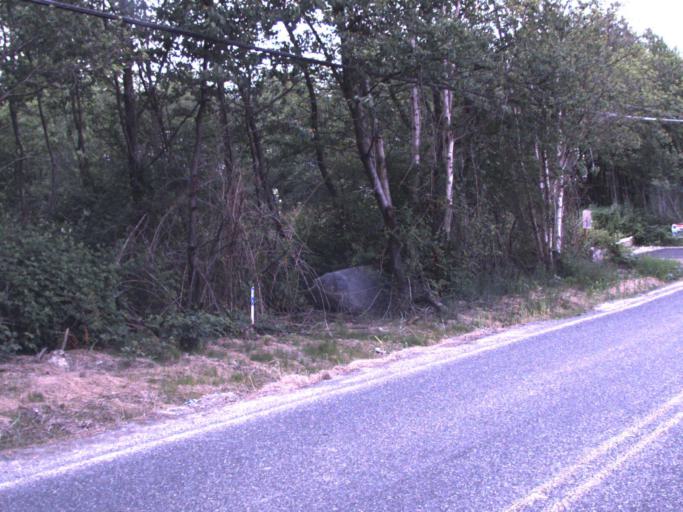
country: US
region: Washington
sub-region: Whatcom County
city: Birch Bay
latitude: 48.9377
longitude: -122.7262
